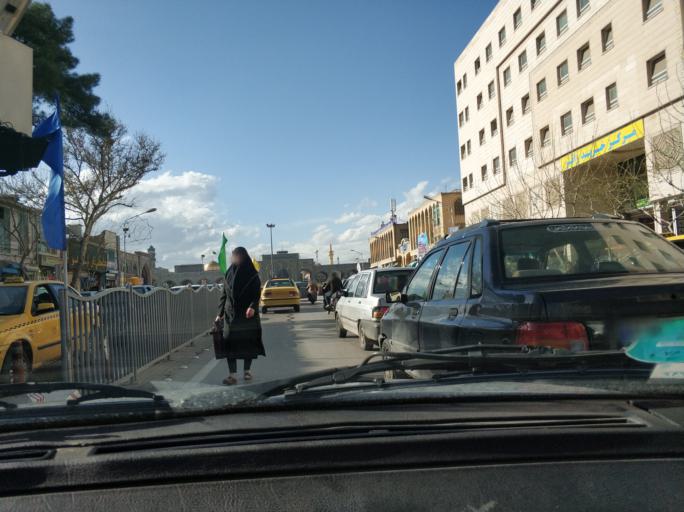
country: IR
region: Razavi Khorasan
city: Mashhad
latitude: 36.2852
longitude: 59.6197
